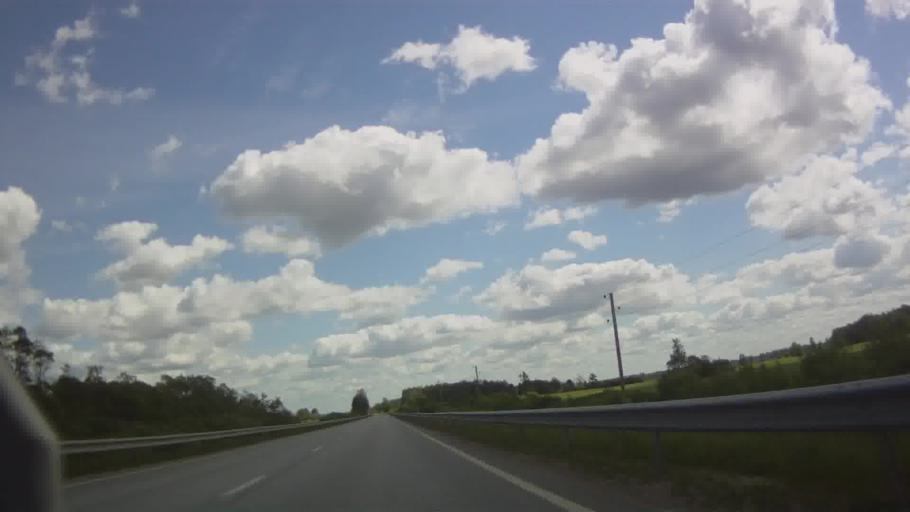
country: LV
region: Livani
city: Livani
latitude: 56.5356
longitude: 26.2810
